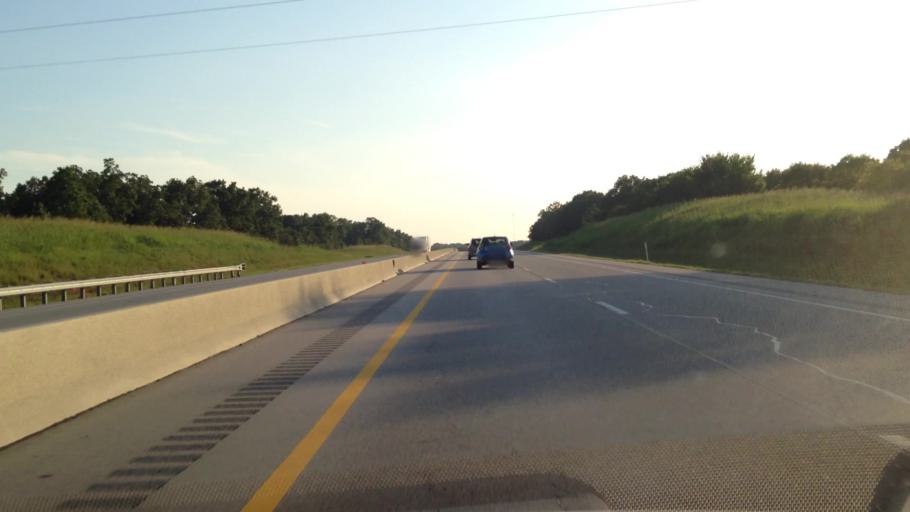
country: US
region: Kansas
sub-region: Cherokee County
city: Baxter Springs
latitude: 36.9489
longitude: -94.6778
